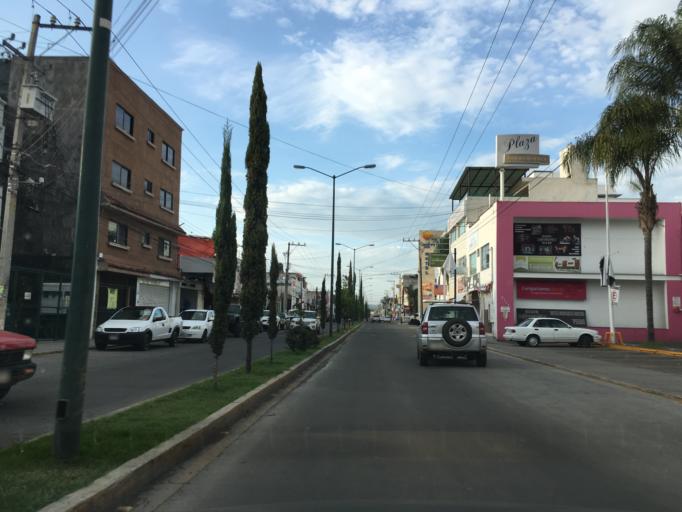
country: MX
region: Michoacan
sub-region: Morelia
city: Morelos
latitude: 19.6799
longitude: -101.2257
